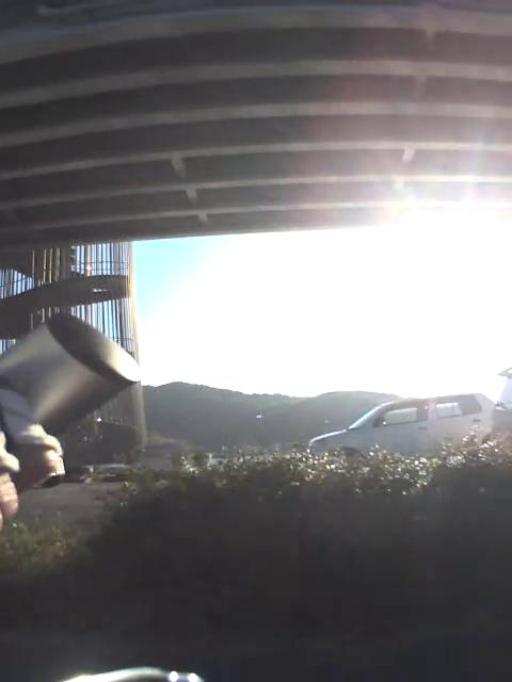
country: JP
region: Yamaguchi
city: Nagato
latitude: 34.3972
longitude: 131.1996
